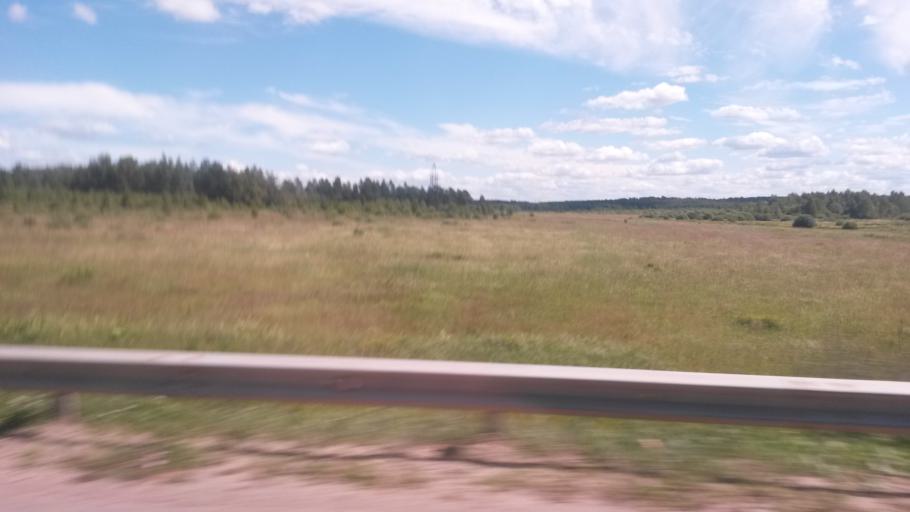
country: RU
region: Ivanovo
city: Rodniki
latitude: 57.1064
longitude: 41.7778
